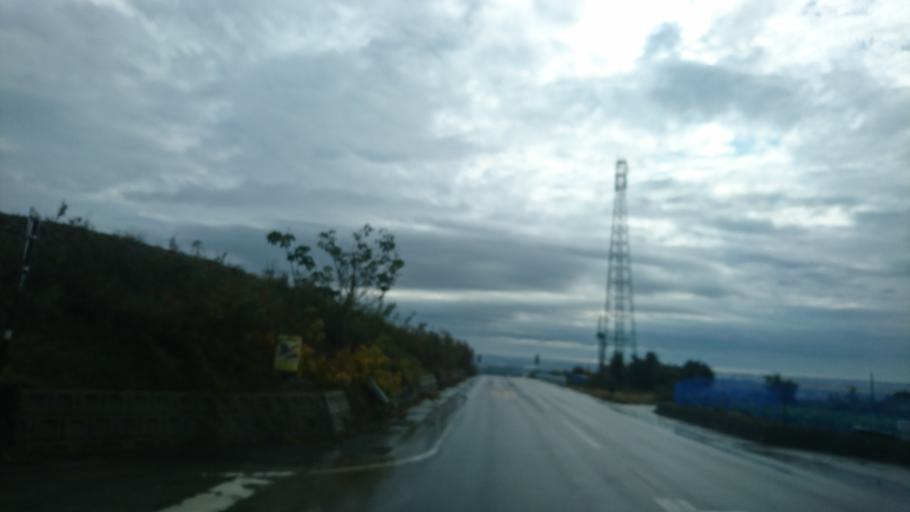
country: JP
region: Shizuoka
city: Fuji
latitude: 35.1707
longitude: 138.7337
